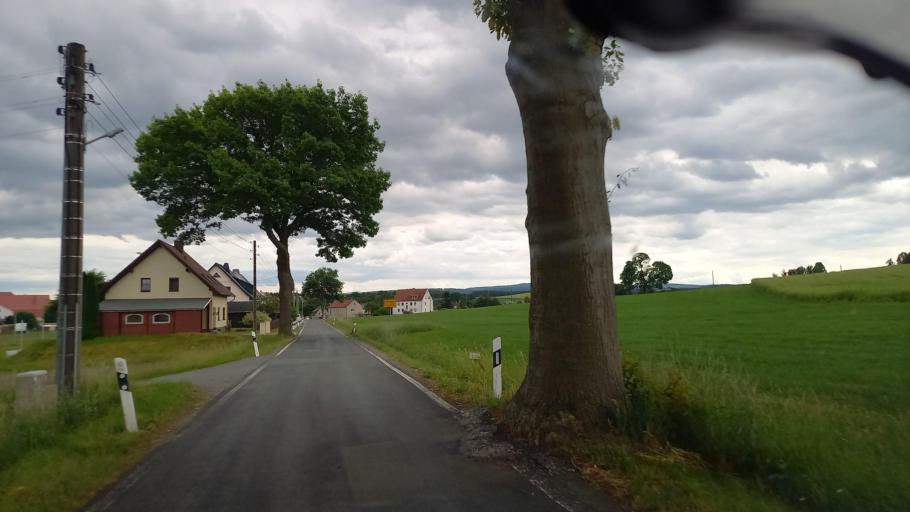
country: DE
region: Saxony
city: Waldkirchen
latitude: 50.6146
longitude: 12.4207
